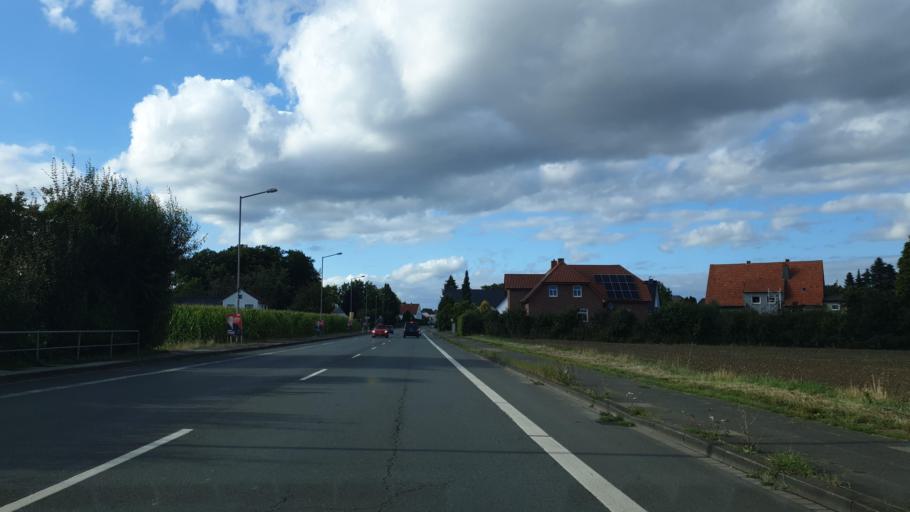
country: DE
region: North Rhine-Westphalia
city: Loehne
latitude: 52.2281
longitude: 8.7039
